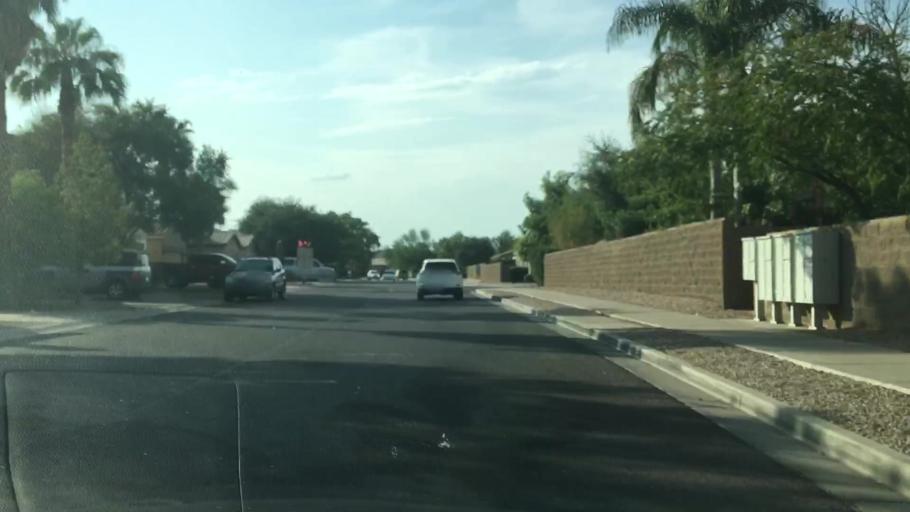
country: US
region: Arizona
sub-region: Pinal County
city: San Tan Valley
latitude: 33.1537
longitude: -111.5594
